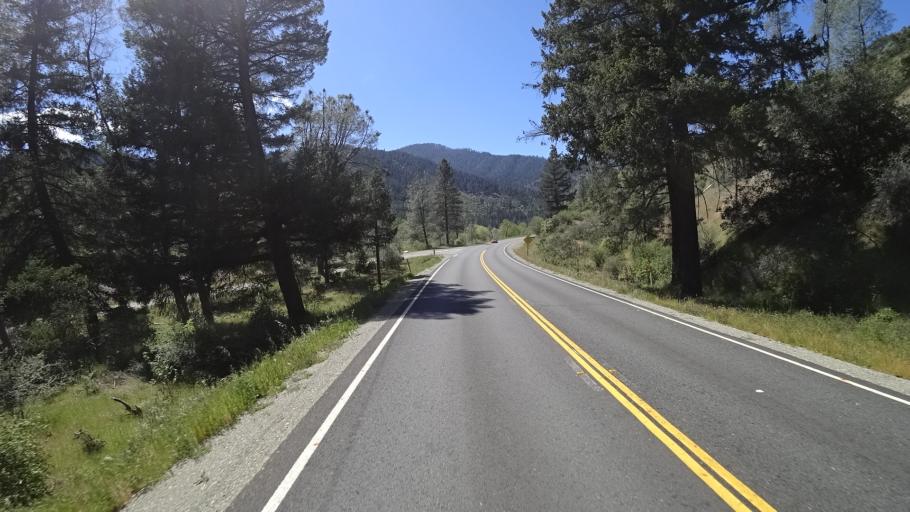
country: US
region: California
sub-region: Trinity County
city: Weaverville
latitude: 40.7251
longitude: -123.0493
